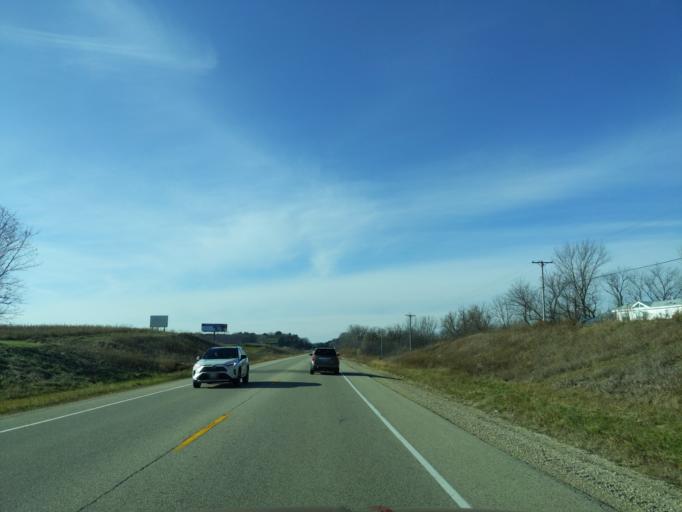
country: US
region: Wisconsin
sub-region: Rock County
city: Milton
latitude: 42.8257
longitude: -88.9905
